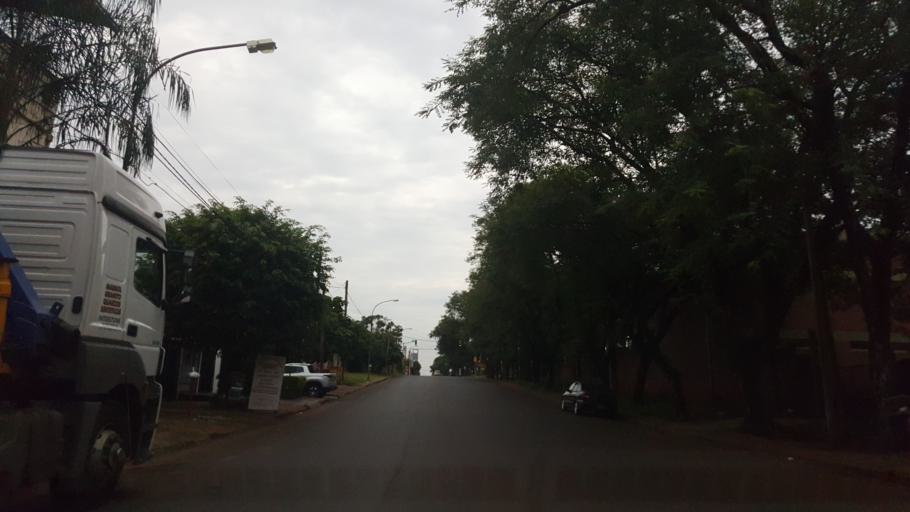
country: AR
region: Misiones
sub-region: Departamento de Capital
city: Posadas
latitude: -27.4029
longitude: -55.8987
